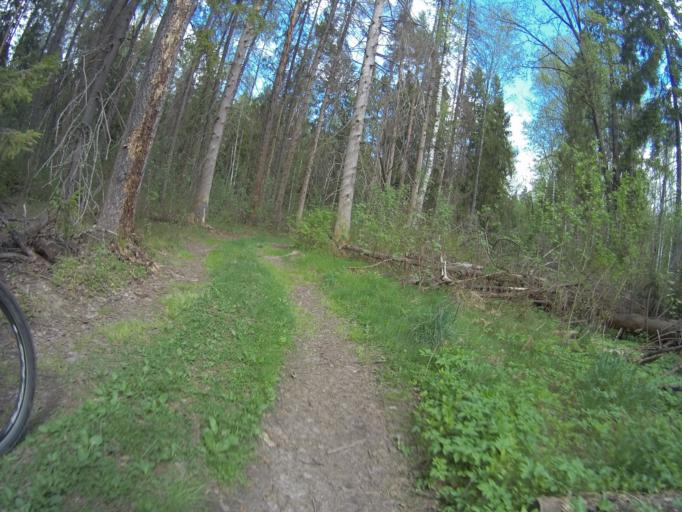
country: RU
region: Vladimir
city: Orgtrud
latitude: 56.1246
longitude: 40.6686
